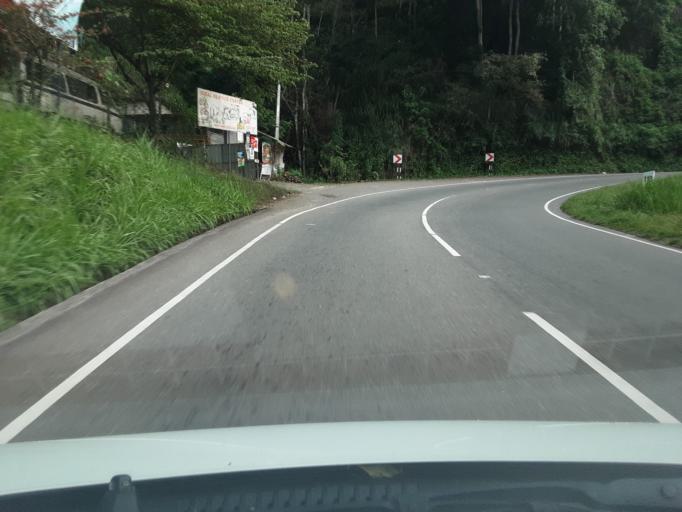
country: LK
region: Uva
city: Badulla
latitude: 6.9477
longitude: 81.0185
